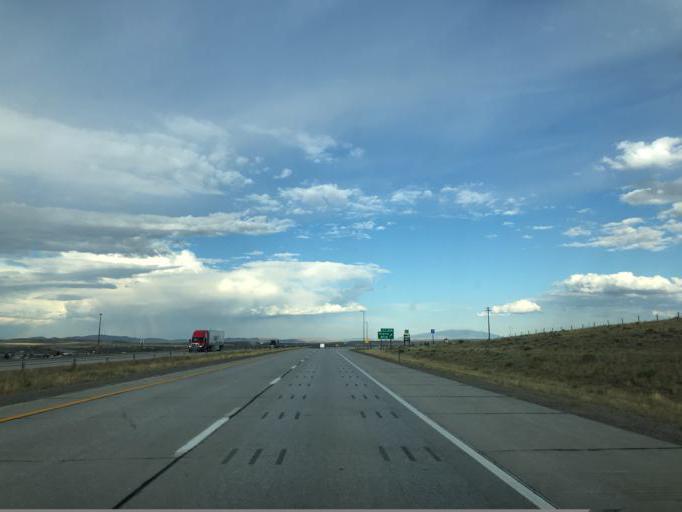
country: US
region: Wyoming
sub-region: Carbon County
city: Rawlins
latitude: 41.7779
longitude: -107.2347
